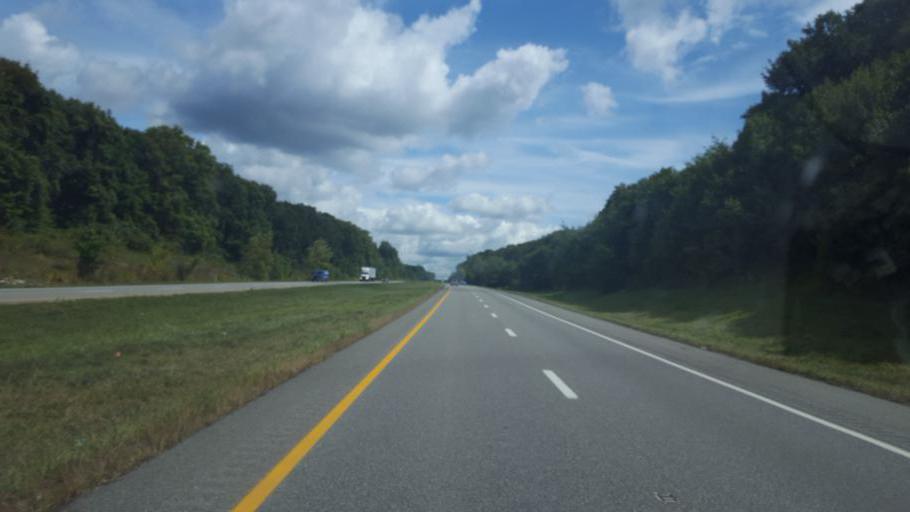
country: US
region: Ohio
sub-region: Geauga County
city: Bainbridge
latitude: 41.3816
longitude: -81.2640
